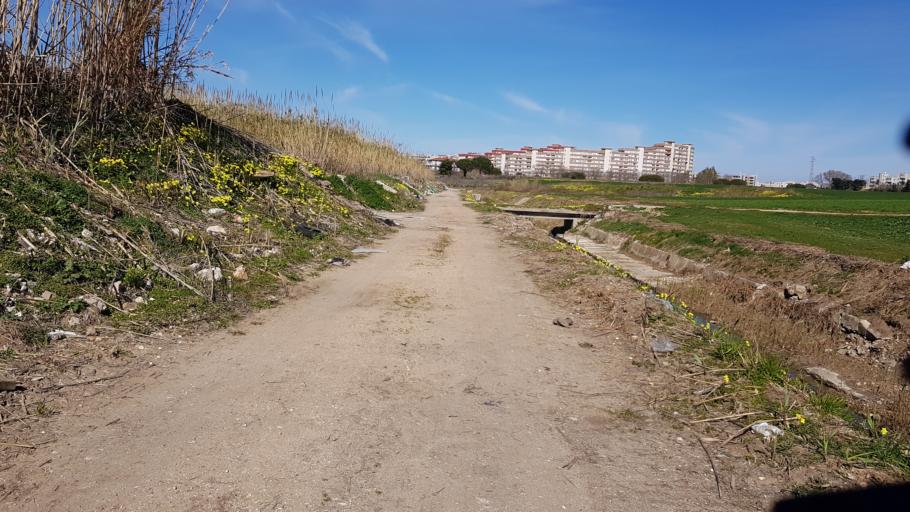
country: IT
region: Apulia
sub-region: Provincia di Brindisi
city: La Rosa
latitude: 40.6155
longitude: 17.9384
